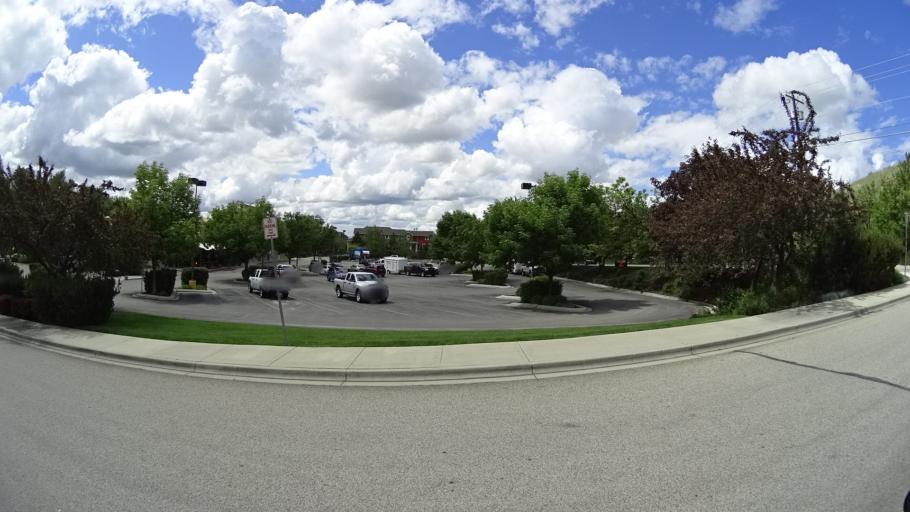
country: US
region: Idaho
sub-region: Ada County
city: Boise
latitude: 43.6441
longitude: -116.2060
